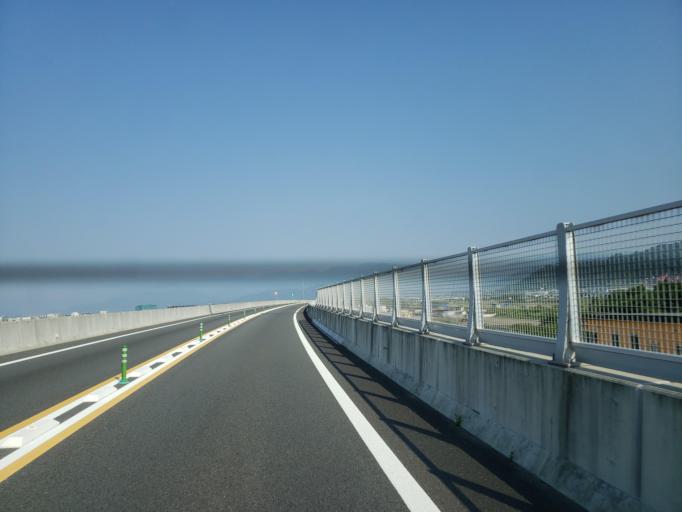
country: JP
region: Ehime
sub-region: Shikoku-chuo Shi
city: Matsuyama
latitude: 33.8050
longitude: 132.7592
